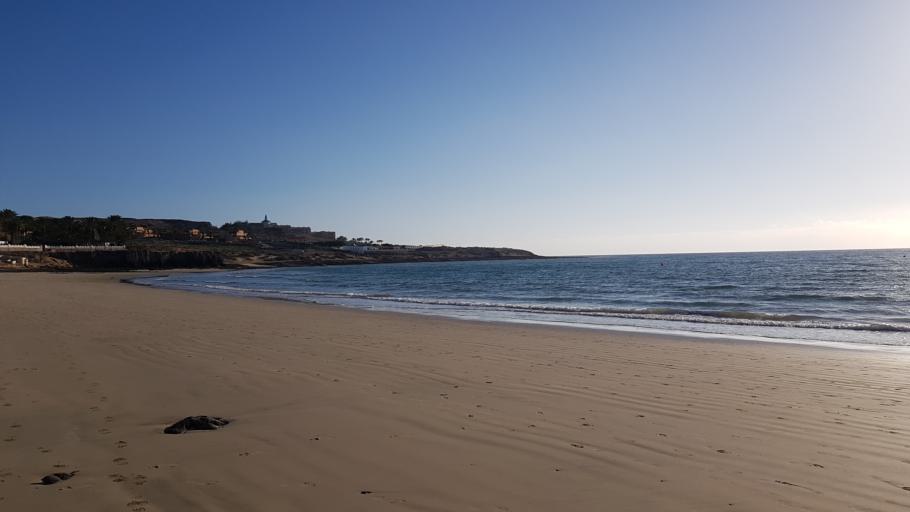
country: ES
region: Canary Islands
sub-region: Provincia de Las Palmas
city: Pajara
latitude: 28.1643
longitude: -14.2201
